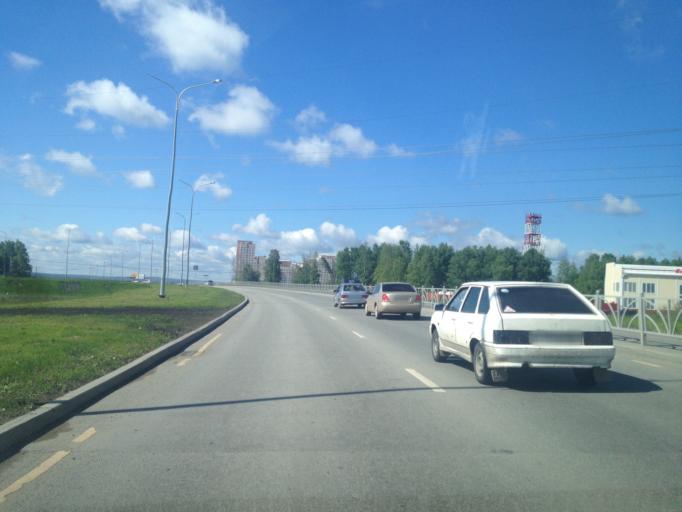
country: RU
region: Sverdlovsk
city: Sovkhoznyy
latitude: 56.7512
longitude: 60.5788
